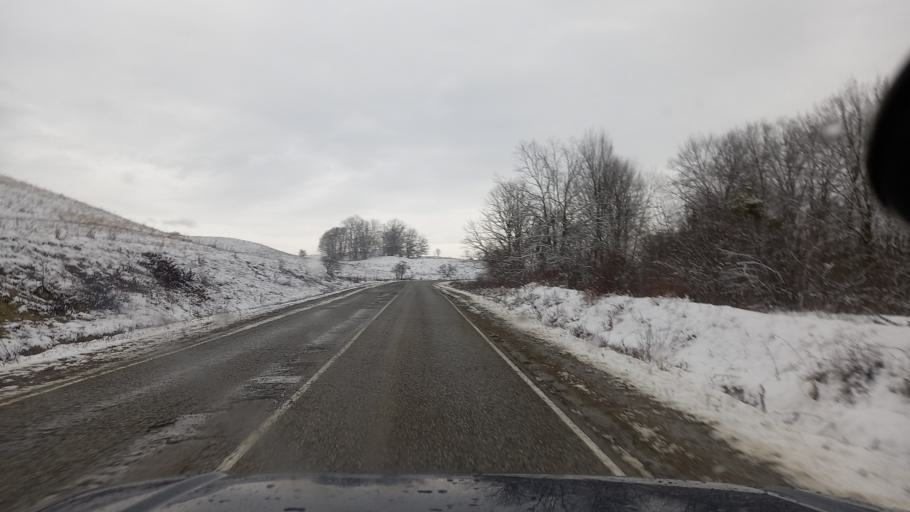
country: RU
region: Adygeya
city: Abadzekhskaya
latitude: 44.3486
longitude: 40.3311
